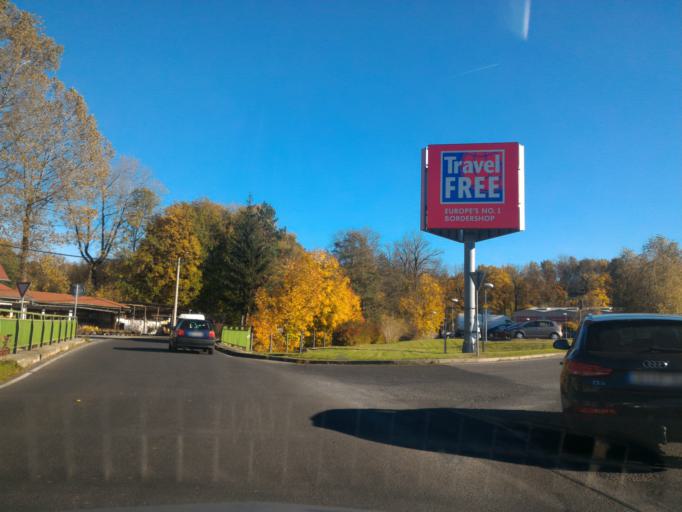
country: CZ
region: Ustecky
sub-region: Okres Decin
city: Sluknov
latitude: 51.0252
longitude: 14.4535
